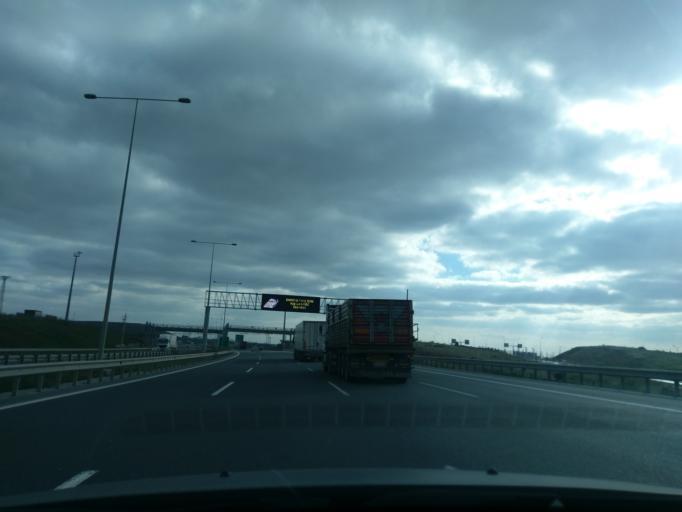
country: TR
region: Istanbul
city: Basaksehir
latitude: 41.1290
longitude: 28.8063
